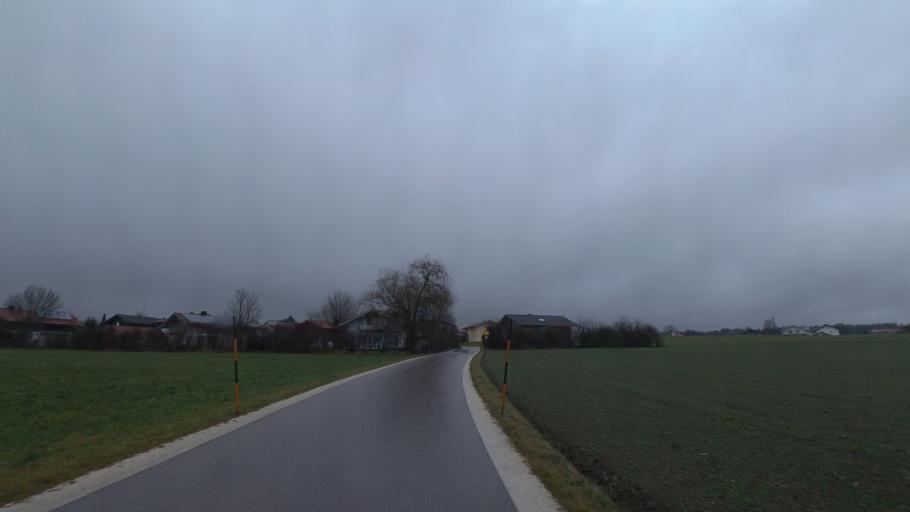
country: DE
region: Bavaria
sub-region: Upper Bavaria
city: Nussdorf
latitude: 47.9228
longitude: 12.6451
